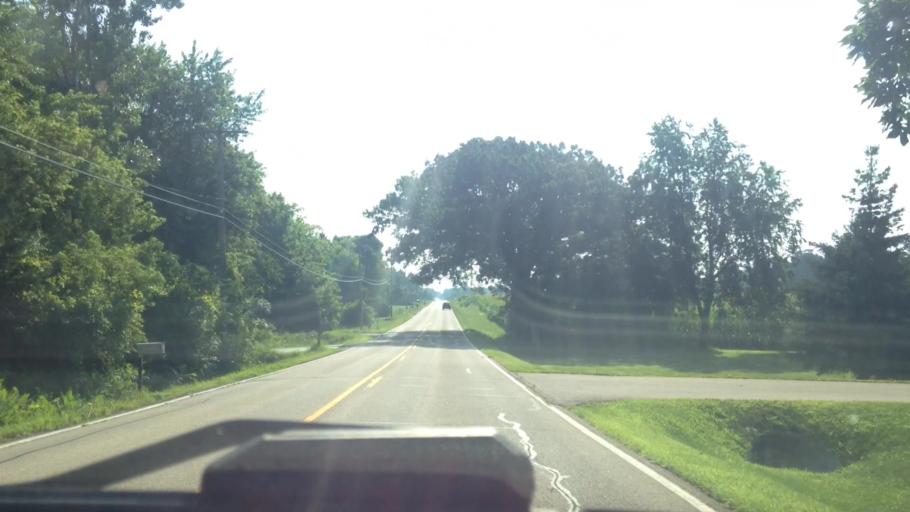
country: US
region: Wisconsin
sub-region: Waukesha County
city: Sussex
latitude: 43.1629
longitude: -88.2339
